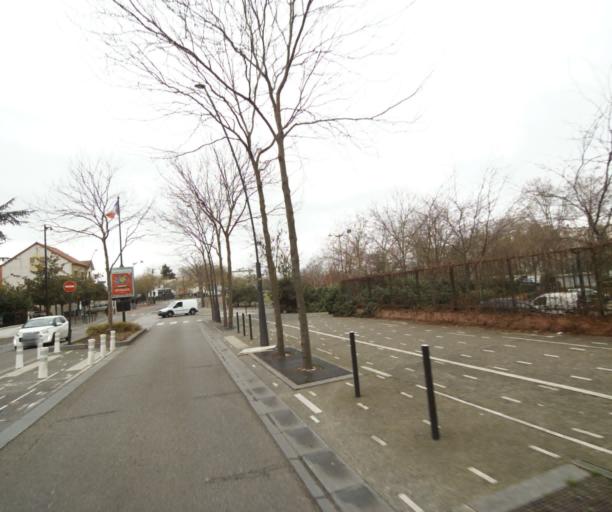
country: FR
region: Ile-de-France
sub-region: Departement des Hauts-de-Seine
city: Rueil-Malmaison
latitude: 48.8630
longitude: 2.1924
